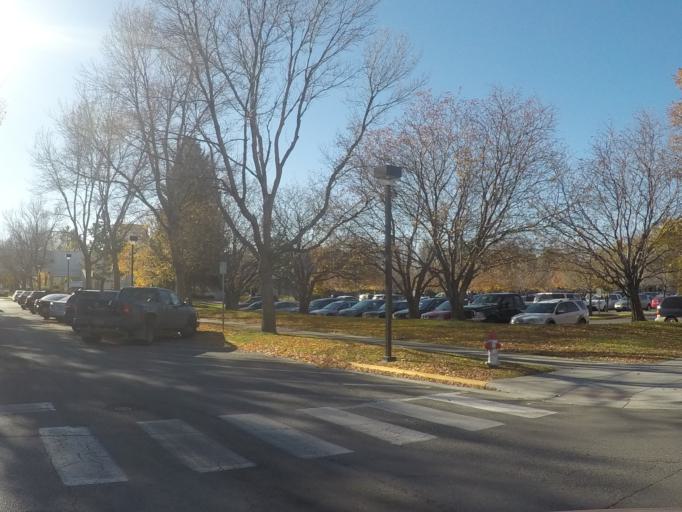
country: US
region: Montana
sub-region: Yellowstone County
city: Billings
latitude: 45.7899
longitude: -108.5153
